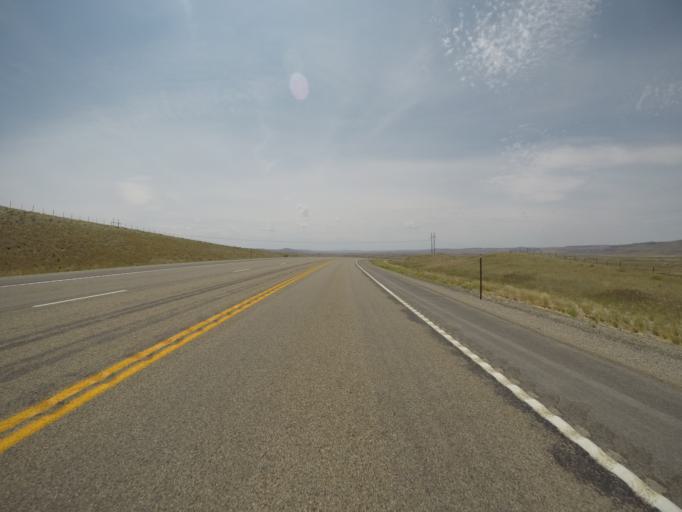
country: US
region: Wyoming
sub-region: Lincoln County
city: Kemmerer
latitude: 41.7603
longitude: -110.5597
